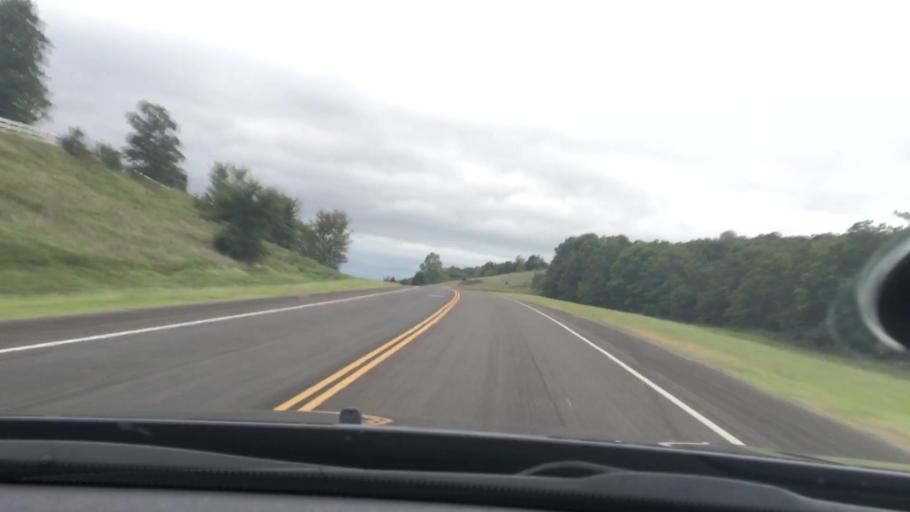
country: US
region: Oklahoma
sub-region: Sequoyah County
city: Vian
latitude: 35.5268
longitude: -94.9745
